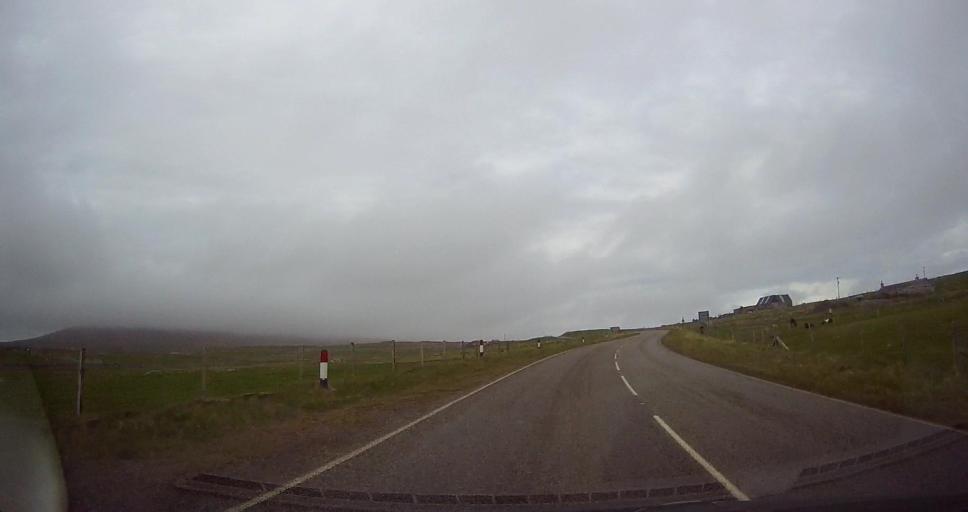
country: GB
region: Scotland
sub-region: Shetland Islands
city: Sandwick
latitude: 59.9291
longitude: -1.2971
